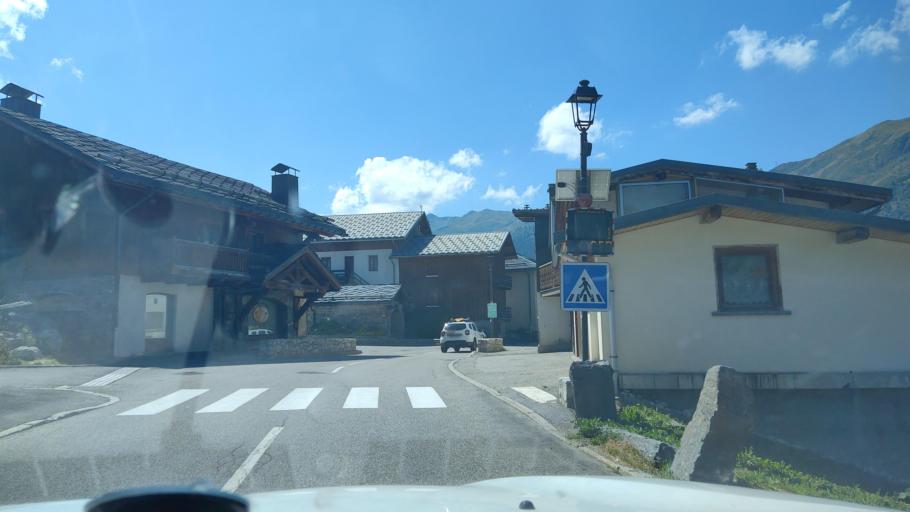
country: FR
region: Rhone-Alpes
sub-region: Departement de la Savoie
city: Meribel
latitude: 45.4166
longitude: 6.5644
